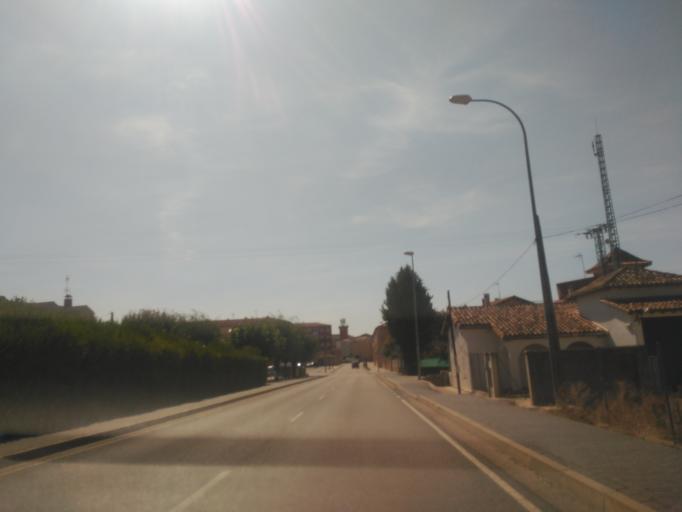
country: ES
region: Castille and Leon
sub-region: Provincia de Soria
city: El Burgo de Osma
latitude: 41.5918
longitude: -3.0620
